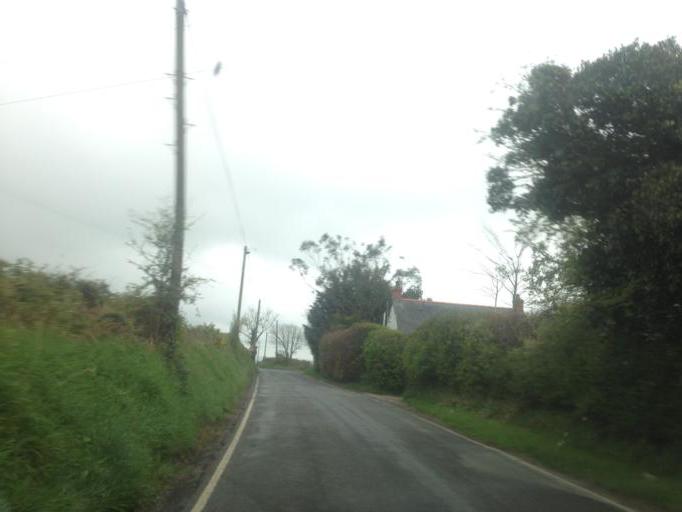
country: GB
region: Wales
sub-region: County of Ceredigion
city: Newcastle Emlyn
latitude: 52.1176
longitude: -4.4413
